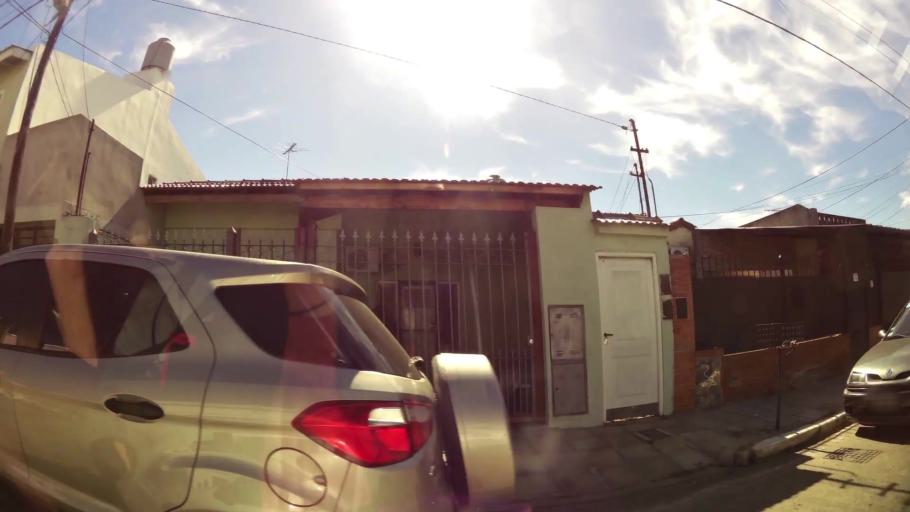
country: AR
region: Buenos Aires
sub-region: Partido de Lomas de Zamora
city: Lomas de Zamora
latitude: -34.7495
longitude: -58.4146
